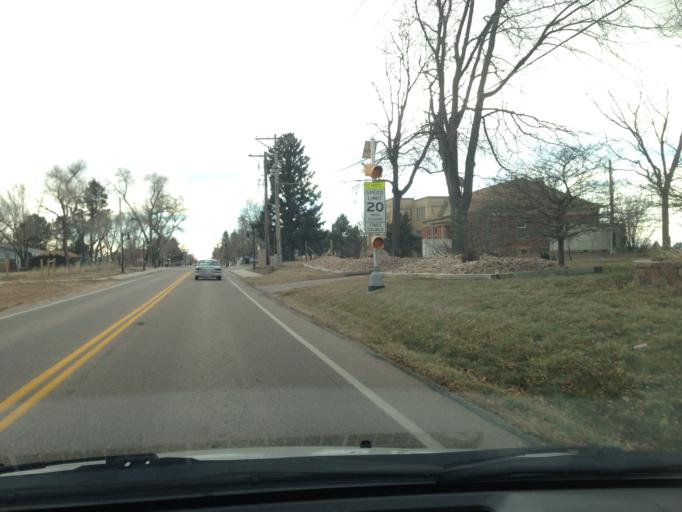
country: US
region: Colorado
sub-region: Weld County
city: Windsor
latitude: 40.5341
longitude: -104.9824
